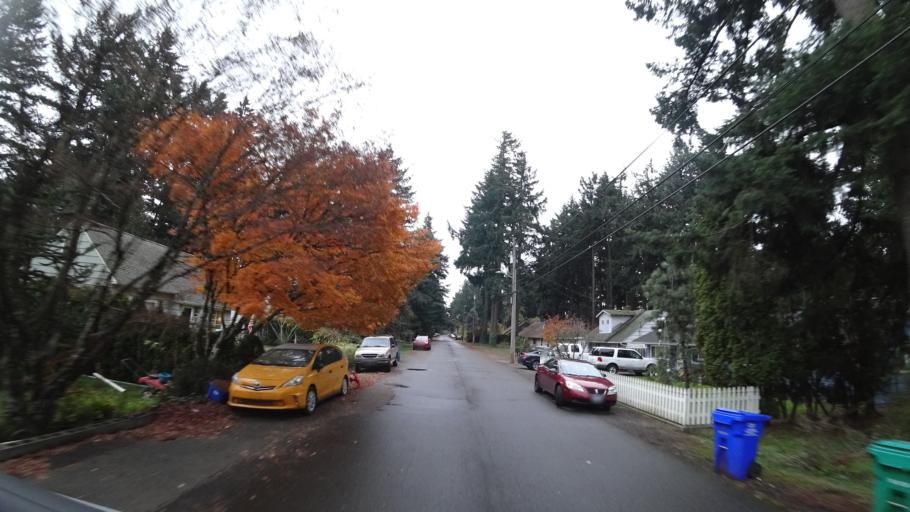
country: US
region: Oregon
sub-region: Multnomah County
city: Lents
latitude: 45.5320
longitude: -122.5472
